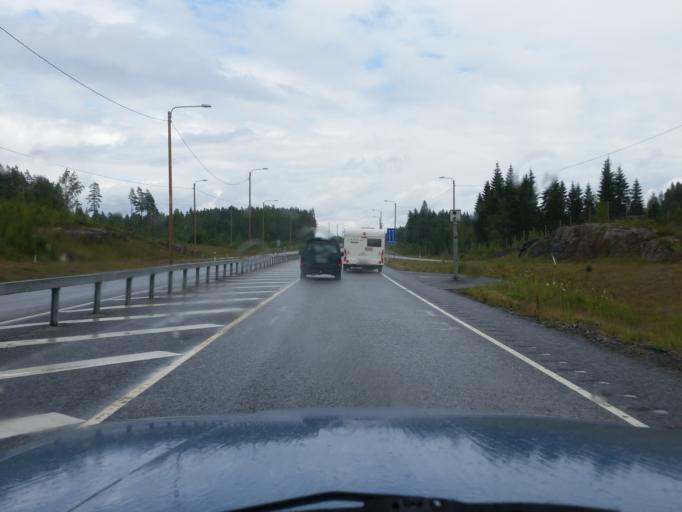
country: FI
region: Southern Savonia
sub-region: Mikkeli
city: Pertunmaa
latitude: 61.4338
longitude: 26.6021
